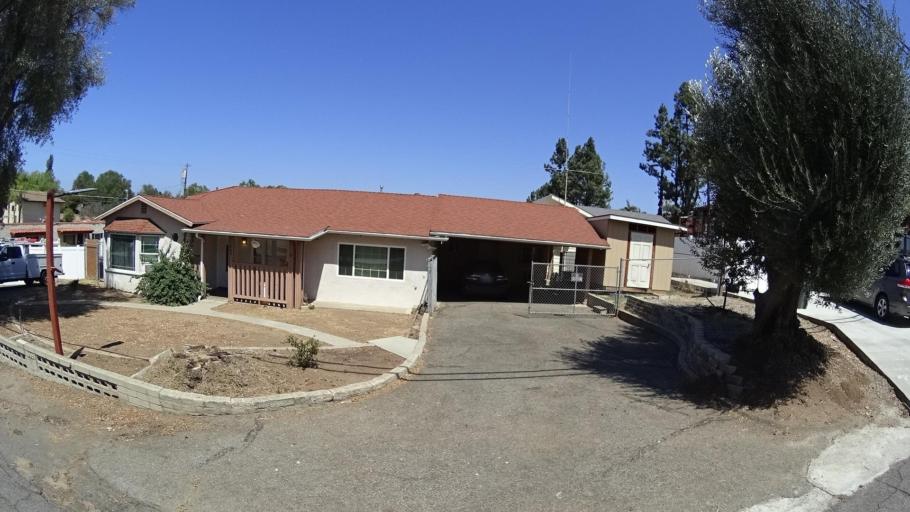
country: US
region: California
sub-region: San Diego County
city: Fallbrook
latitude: 33.3820
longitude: -117.2428
